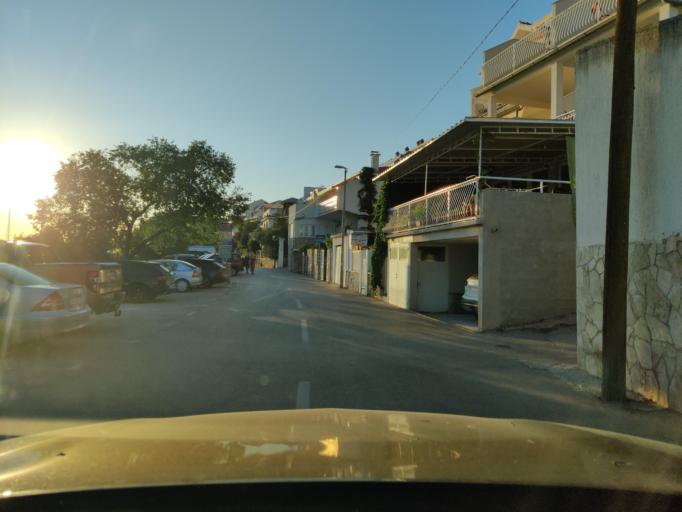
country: HR
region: Sibensko-Kniniska
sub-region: Grad Sibenik
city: Tisno
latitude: 43.8041
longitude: 15.6340
